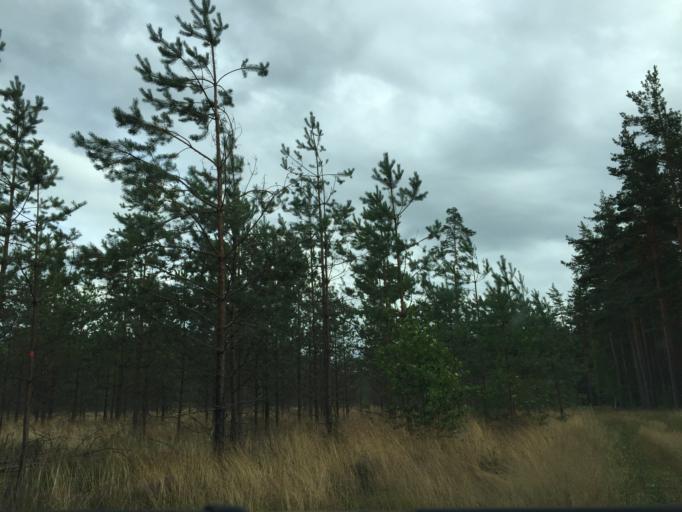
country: LV
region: Saulkrastu
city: Saulkrasti
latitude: 57.2125
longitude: 24.4254
